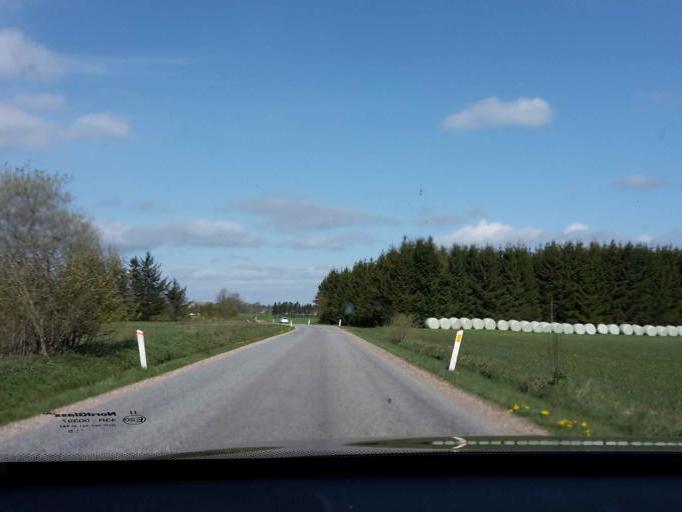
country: DK
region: South Denmark
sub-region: Vejen Kommune
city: Holsted
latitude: 55.5801
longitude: 8.9779
